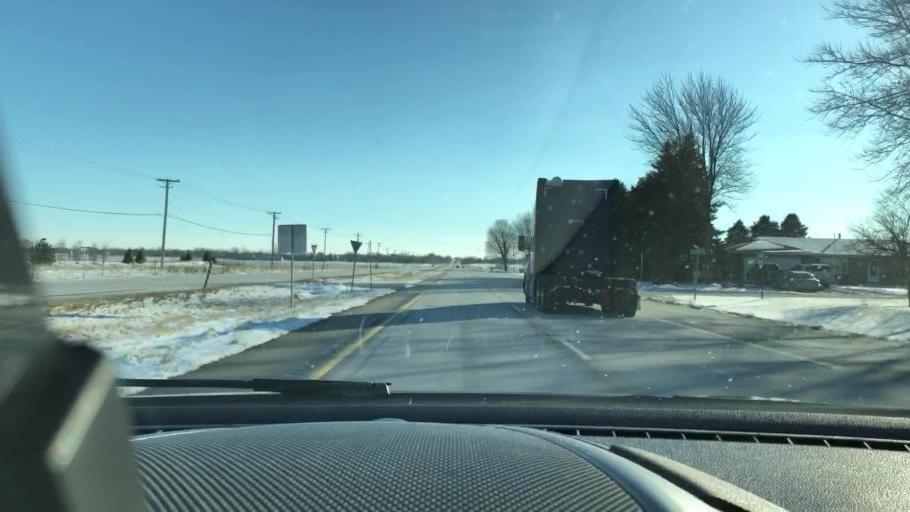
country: US
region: Illinois
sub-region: Will County
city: Preston Heights
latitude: 41.4496
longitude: -88.0792
